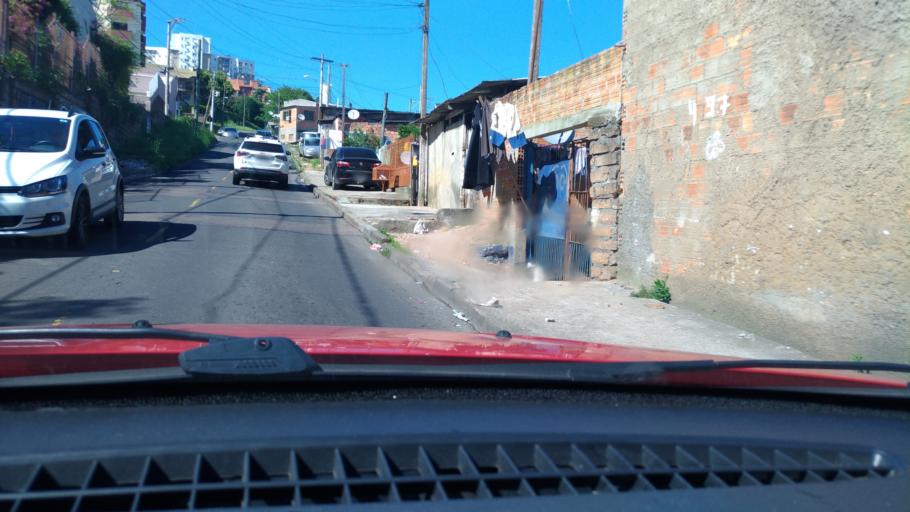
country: BR
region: Rio Grande do Sul
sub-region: Porto Alegre
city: Porto Alegre
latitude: -30.0321
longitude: -51.1478
